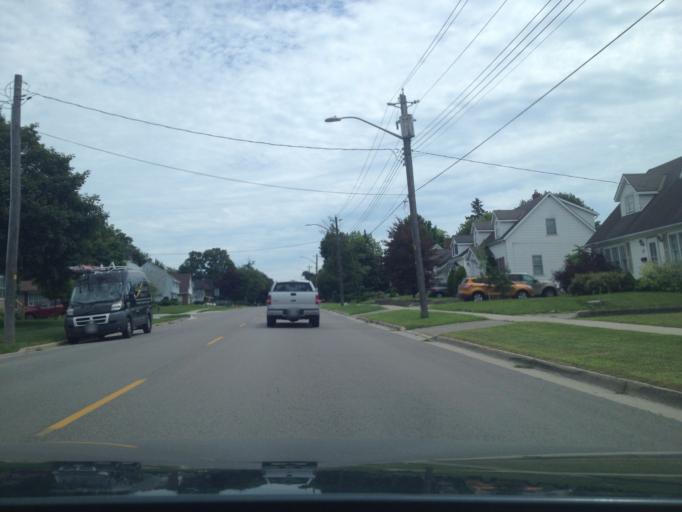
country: CA
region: Ontario
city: Norfolk County
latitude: 42.8542
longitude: -80.4913
